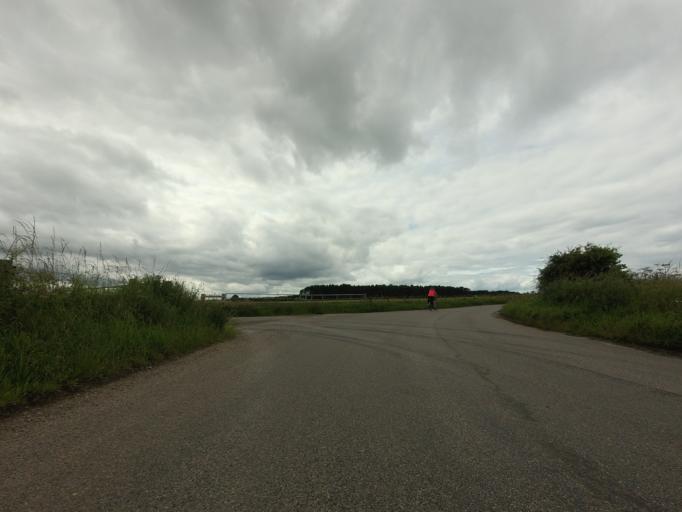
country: GB
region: Scotland
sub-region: Moray
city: Forres
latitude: 57.6213
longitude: -3.6629
